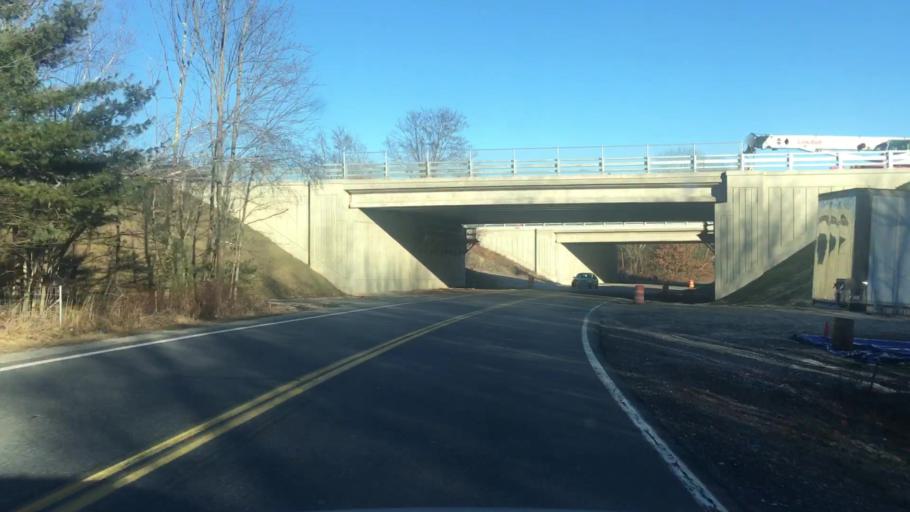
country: US
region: New Hampshire
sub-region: Rockingham County
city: Londonderry
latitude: 42.9025
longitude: -71.3646
